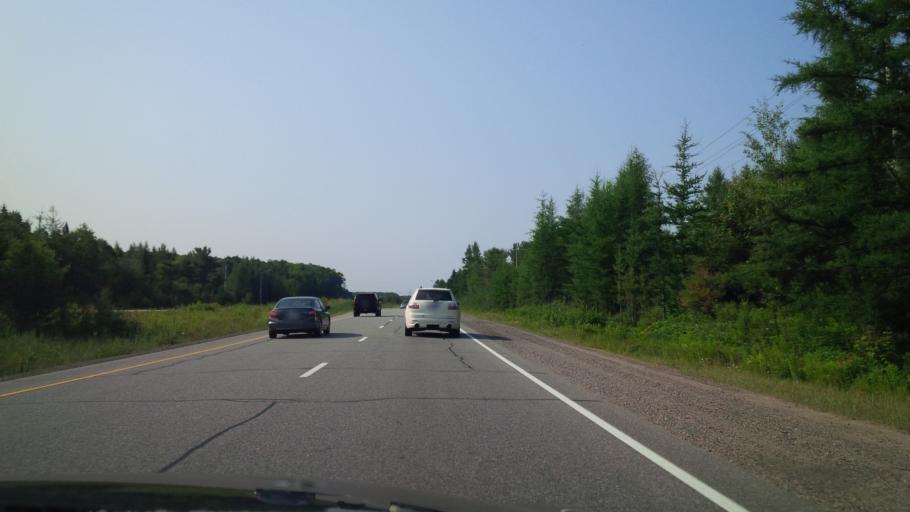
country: CA
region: Ontario
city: Bracebridge
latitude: 45.1794
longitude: -79.3125
